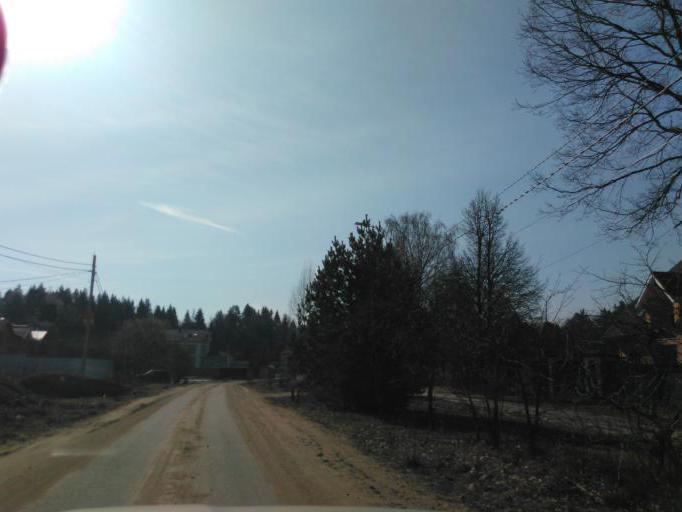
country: RU
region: Moskovskaya
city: Opalikha
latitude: 55.8748
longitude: 37.2717
